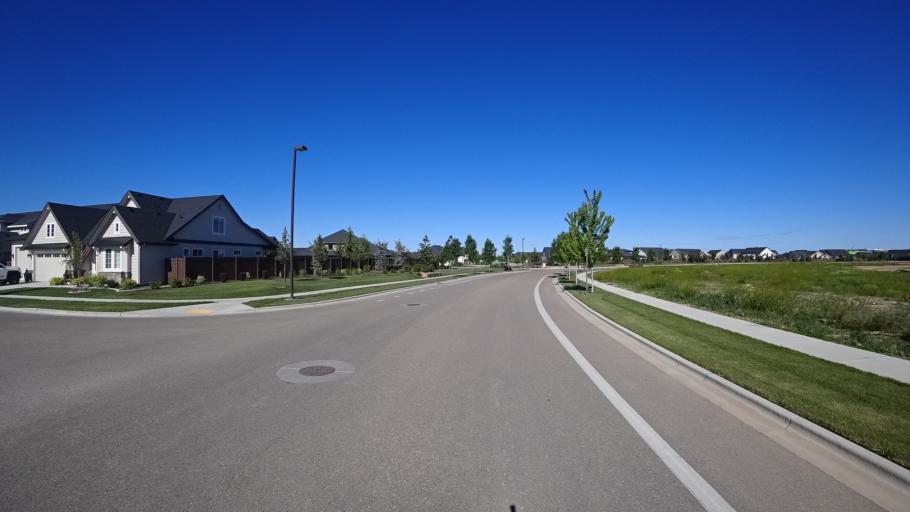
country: US
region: Idaho
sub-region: Ada County
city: Star
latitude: 43.6596
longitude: -116.4419
